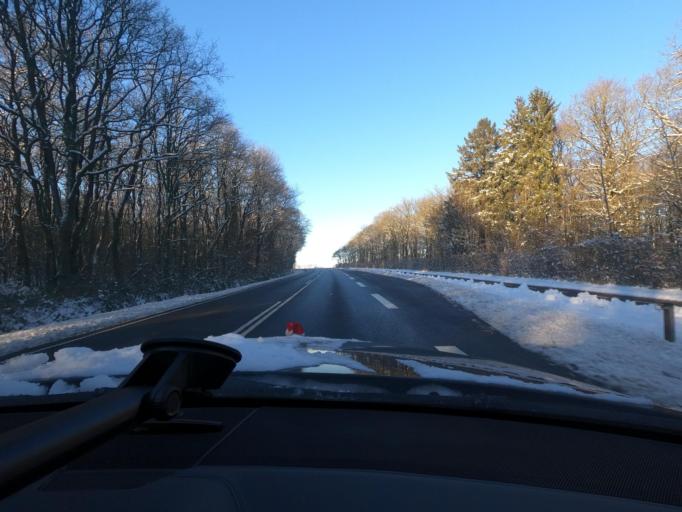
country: DK
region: South Denmark
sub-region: Tonder Kommune
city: Toftlund
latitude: 55.1454
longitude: 9.1147
